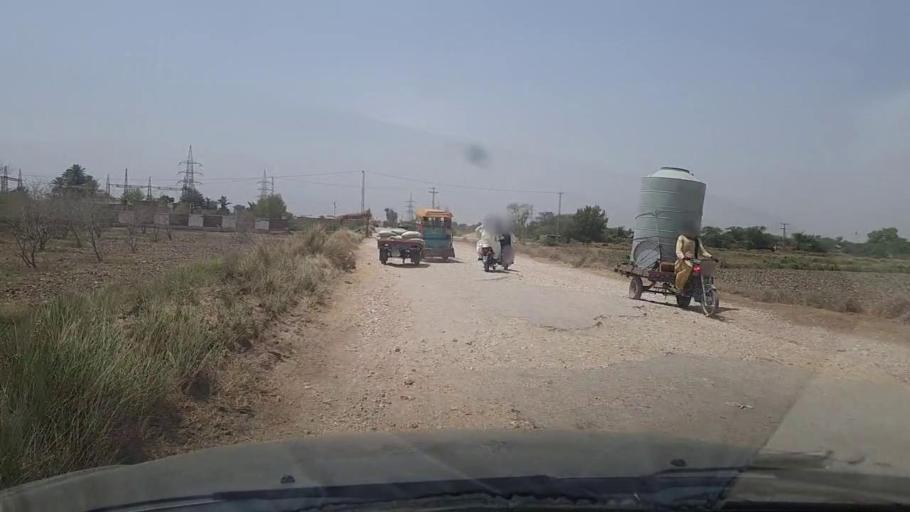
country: PK
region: Sindh
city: Karaundi
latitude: 26.8784
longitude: 68.3184
